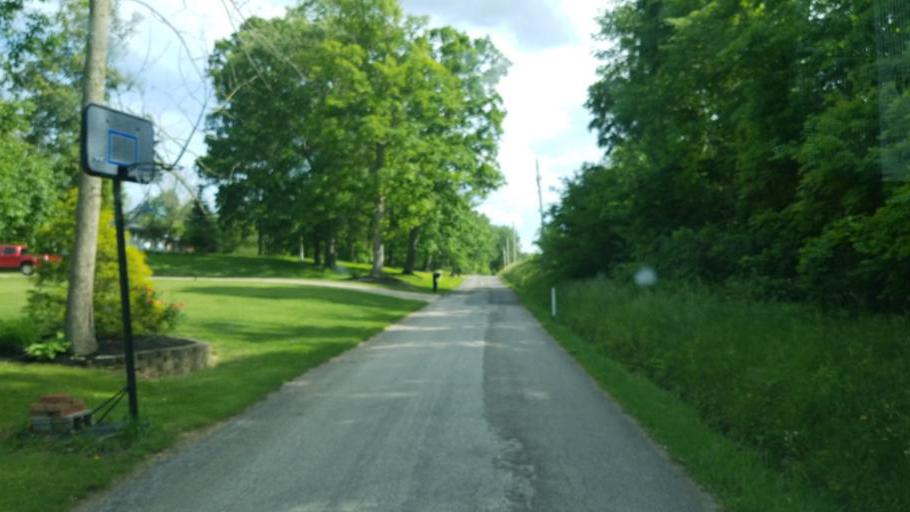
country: US
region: Ohio
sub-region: Richland County
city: Lincoln Heights
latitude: 40.8427
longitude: -82.5013
